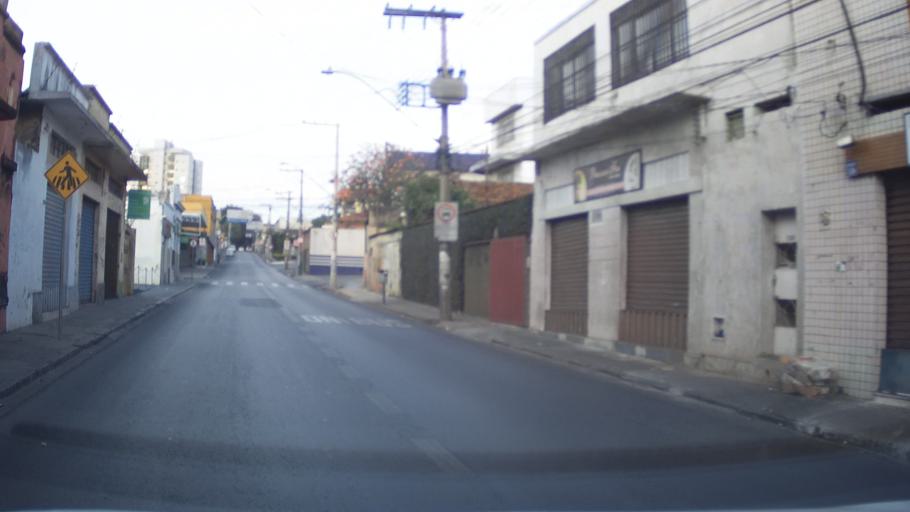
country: BR
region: Minas Gerais
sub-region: Belo Horizonte
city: Belo Horizonte
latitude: -19.9127
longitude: -43.9659
